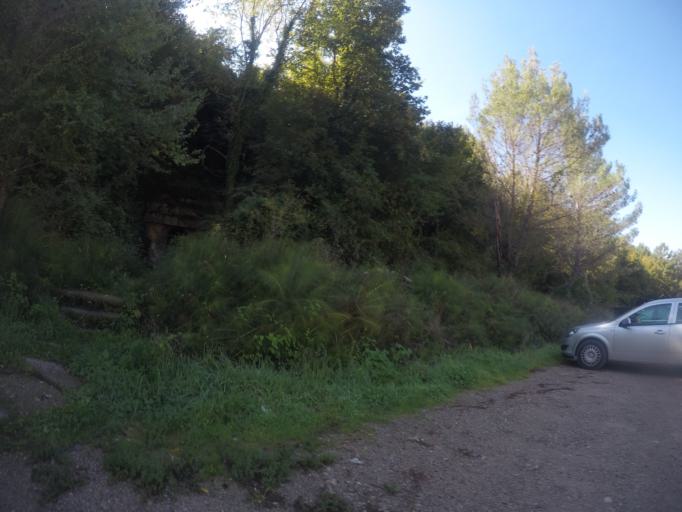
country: AL
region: Tirane
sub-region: Rrethi i Tiranes
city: Farka e Madhe
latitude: 41.3515
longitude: 19.8605
